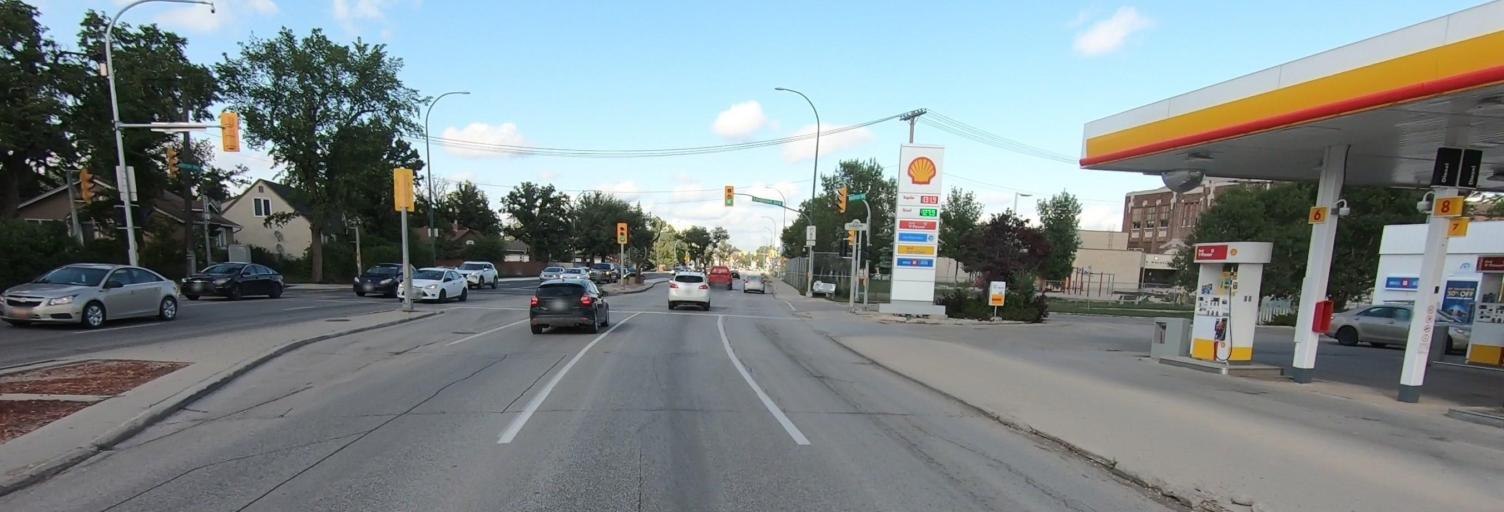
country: CA
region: Manitoba
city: Winnipeg
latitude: 49.9327
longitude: -97.0991
